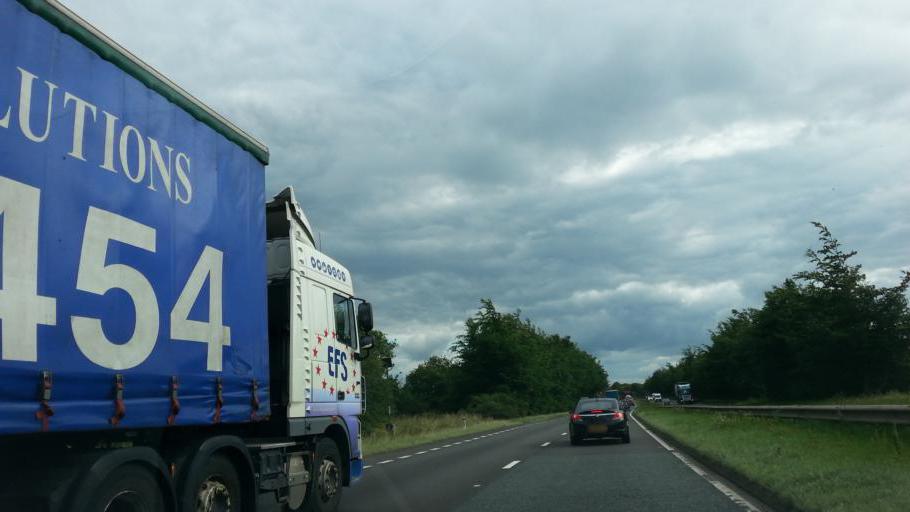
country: GB
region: England
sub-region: Nottinghamshire
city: Babworth
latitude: 53.3069
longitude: -1.0303
